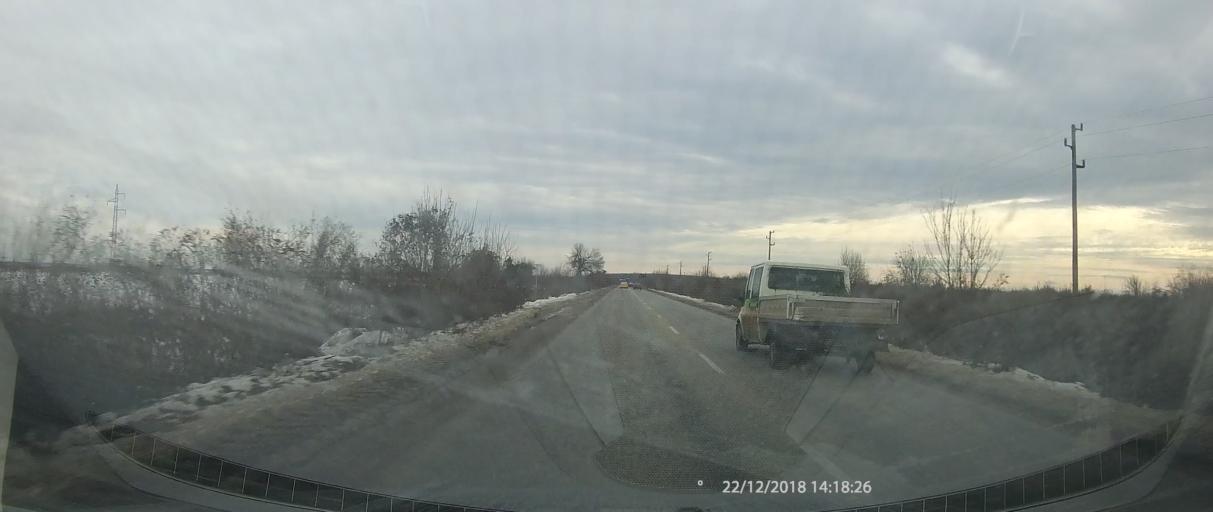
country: BG
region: Pleven
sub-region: Obshtina Pleven
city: Pleven
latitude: 43.4233
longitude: 24.7168
